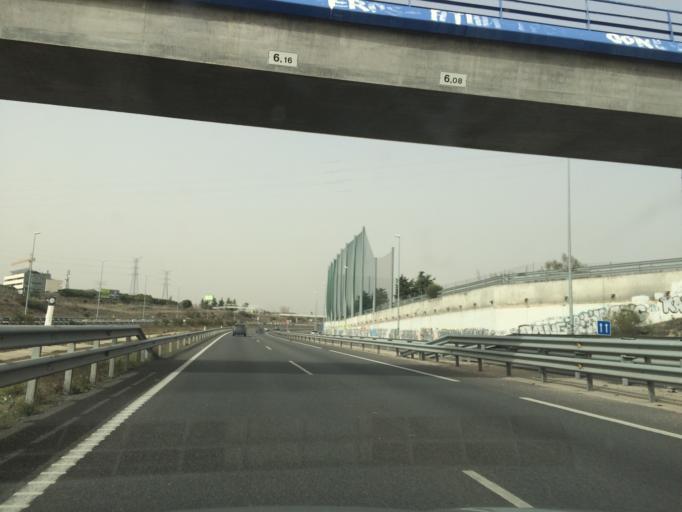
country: ES
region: Madrid
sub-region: Provincia de Madrid
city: Majadahonda
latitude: 40.4439
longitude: -3.8784
